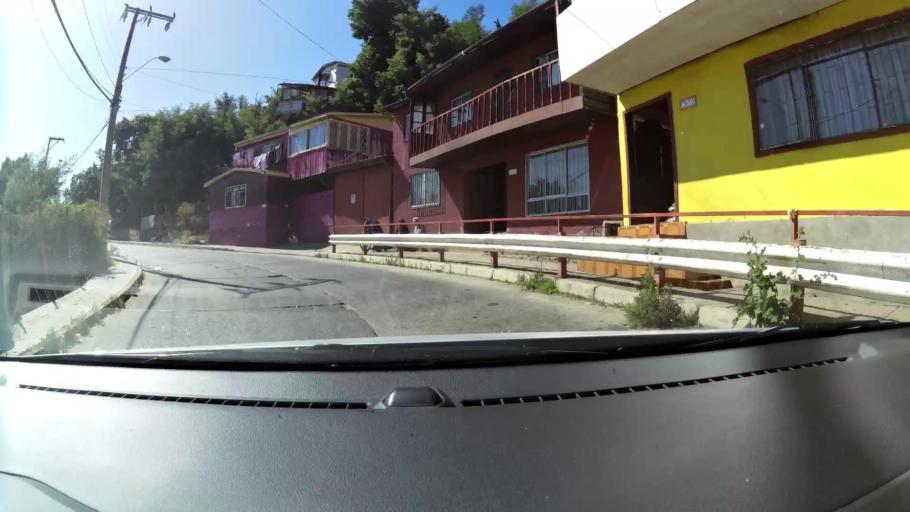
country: CL
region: Valparaiso
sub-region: Provincia de Valparaiso
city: Valparaiso
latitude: -33.0652
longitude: -71.5910
